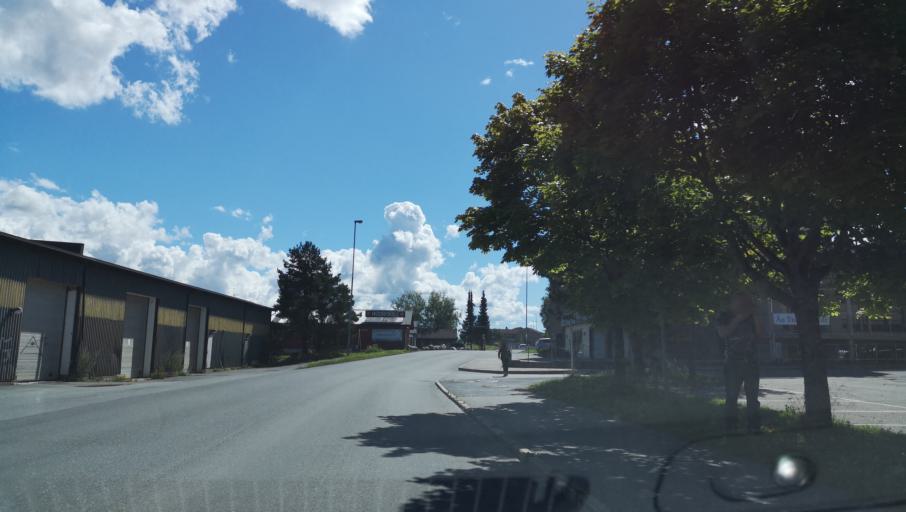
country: NO
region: Akershus
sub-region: As
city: As
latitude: 59.6618
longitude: 10.7942
